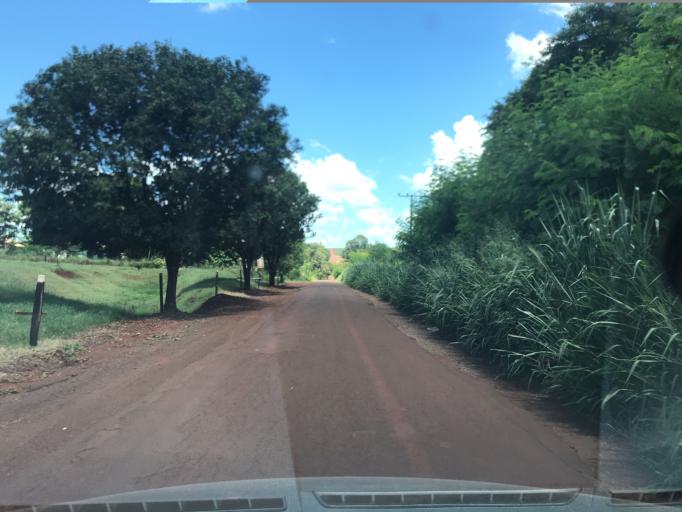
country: BR
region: Parana
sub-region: Palotina
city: Palotina
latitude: -24.2955
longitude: -53.8601
